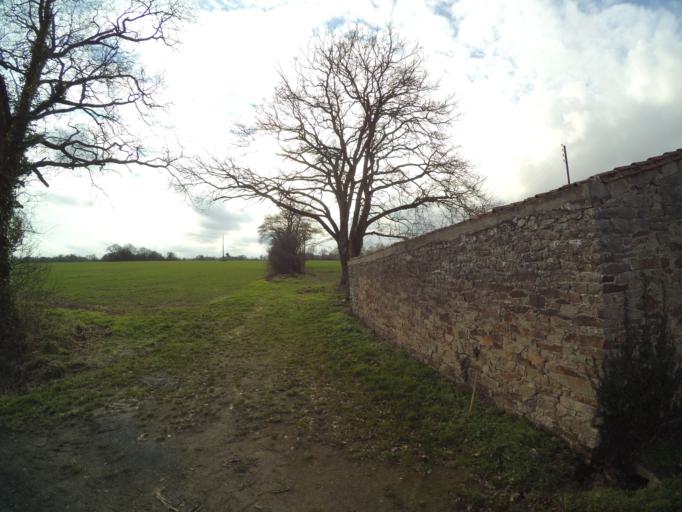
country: FR
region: Pays de la Loire
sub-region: Departement de la Loire-Atlantique
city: Clisson
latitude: 47.0748
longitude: -1.2789
